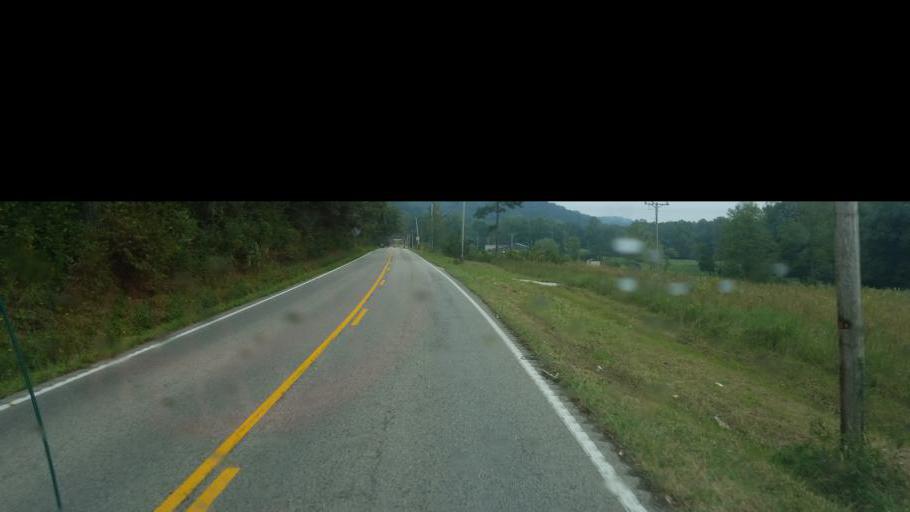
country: US
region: Kentucky
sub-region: Rowan County
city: Morehead
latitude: 38.2669
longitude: -83.4295
